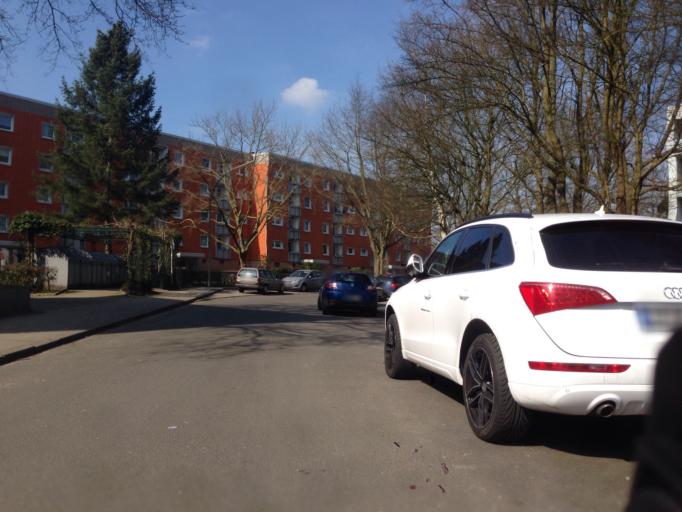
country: DE
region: Schleswig-Holstein
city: Barsbuettel
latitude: 53.5780
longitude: 10.1457
